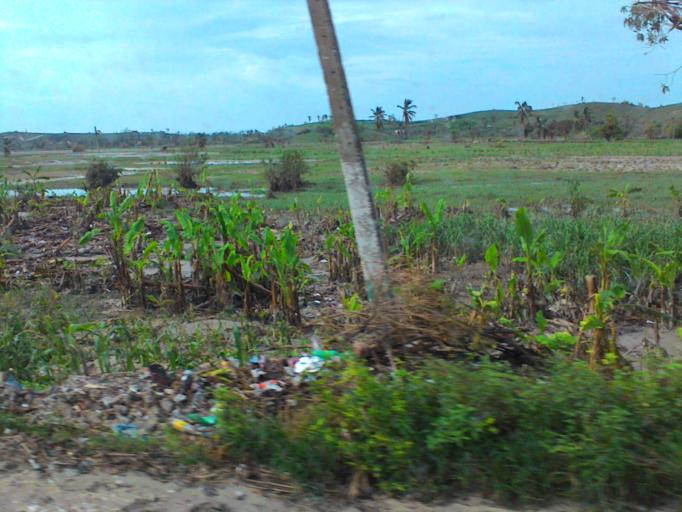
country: HT
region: Sud
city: Les Cayes
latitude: 18.2477
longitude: -73.7426
